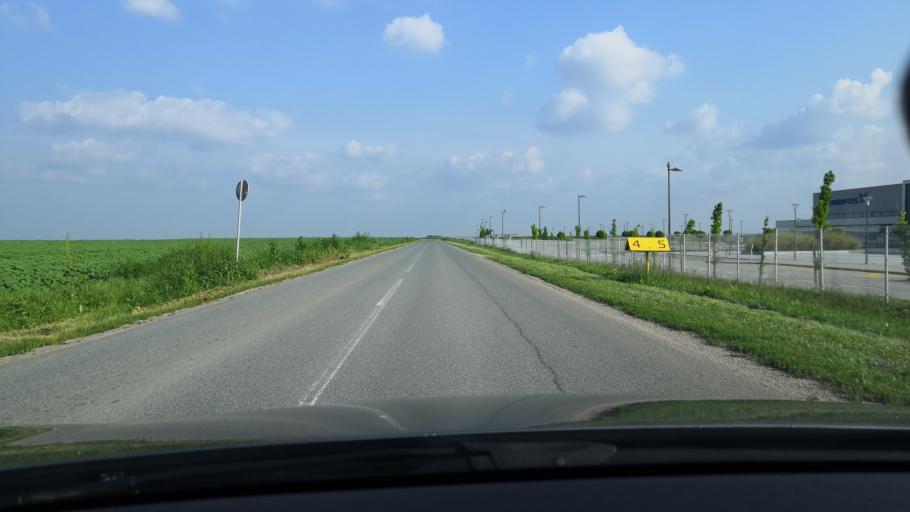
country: RS
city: Beska
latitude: 45.0943
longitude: 20.0952
